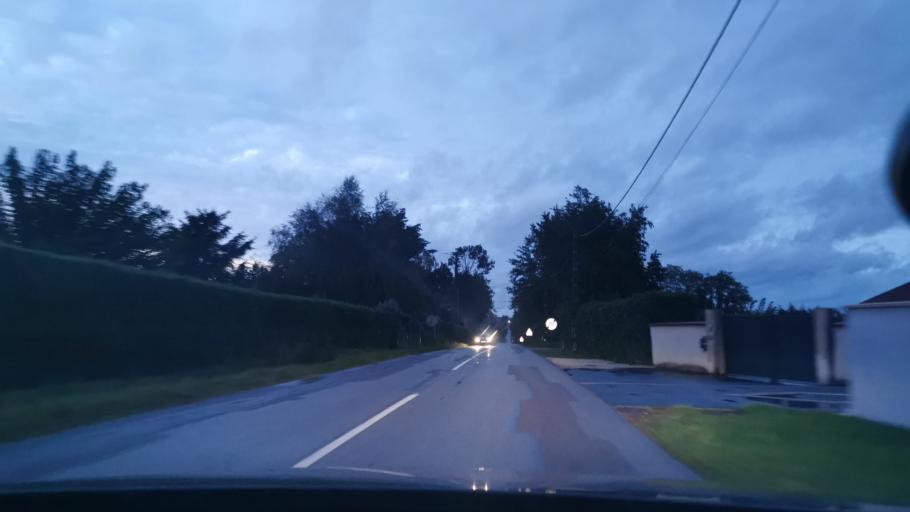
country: FR
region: Rhone-Alpes
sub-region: Departement de l'Ain
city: Bage-la-Ville
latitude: 46.3377
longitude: 4.9380
